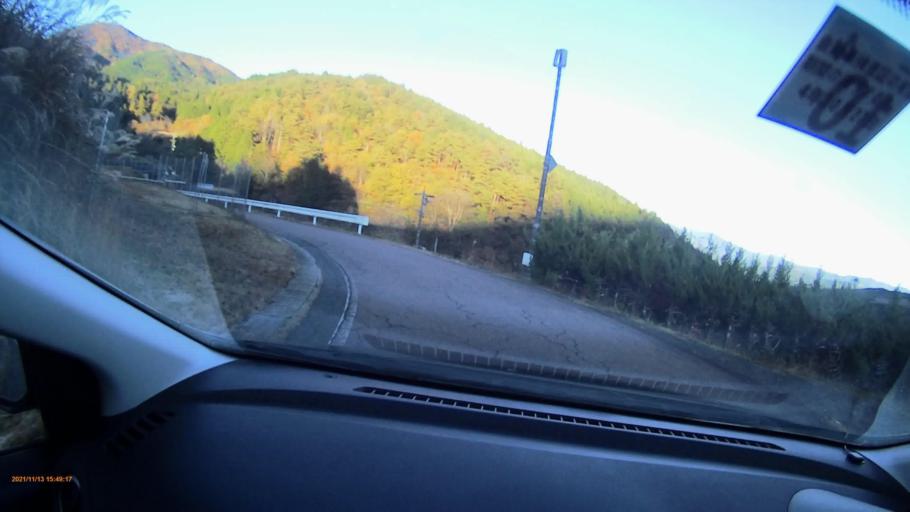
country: JP
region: Gifu
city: Nakatsugawa
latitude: 35.5975
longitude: 137.4080
